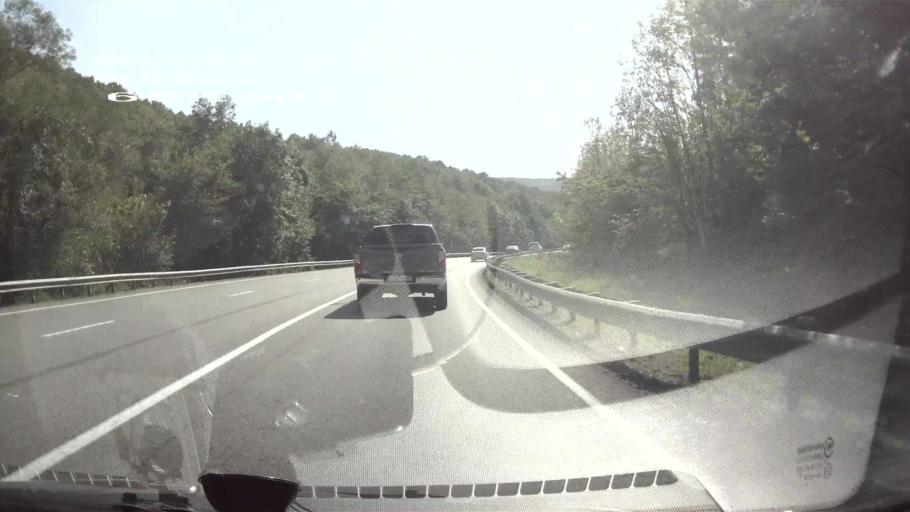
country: RU
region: Krasnodarskiy
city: Goryachiy Klyuch
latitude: 44.5680
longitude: 39.0029
